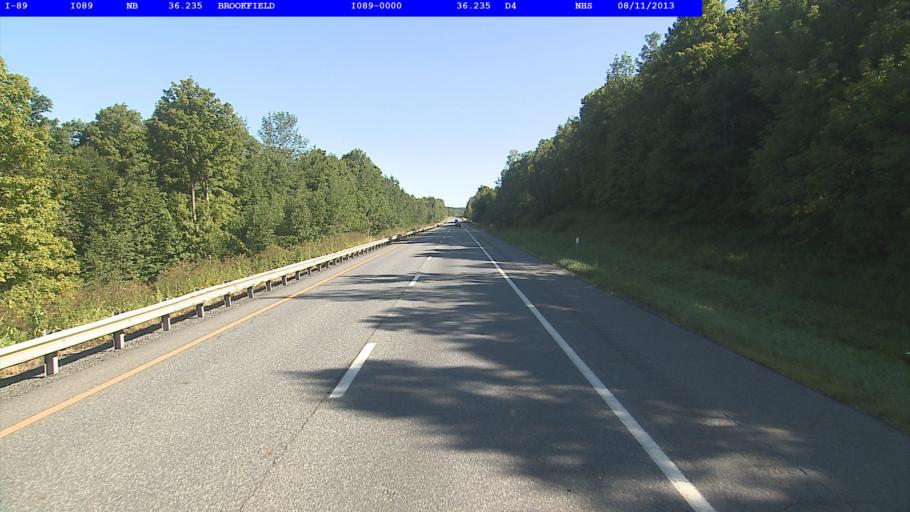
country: US
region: Vermont
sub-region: Orange County
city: Randolph
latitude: 44.0209
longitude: -72.6165
